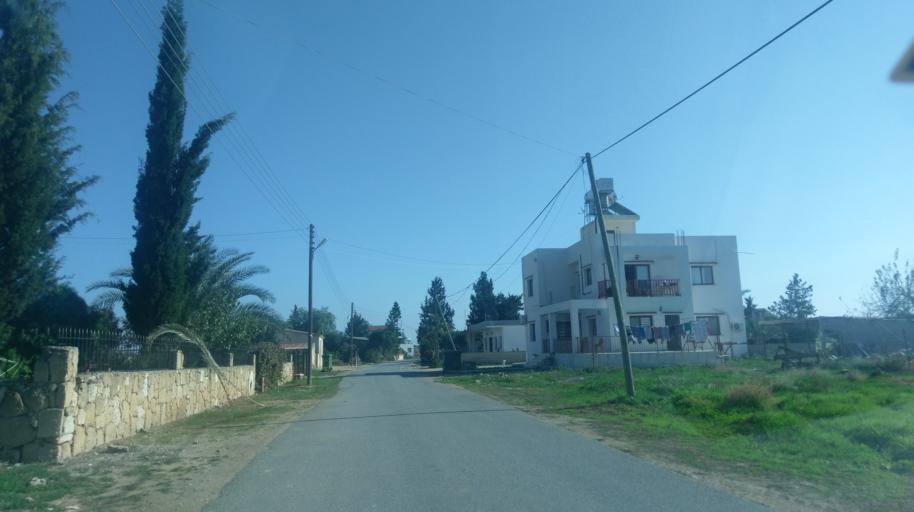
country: CY
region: Ammochostos
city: Trikomo
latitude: 35.2385
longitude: 33.8550
